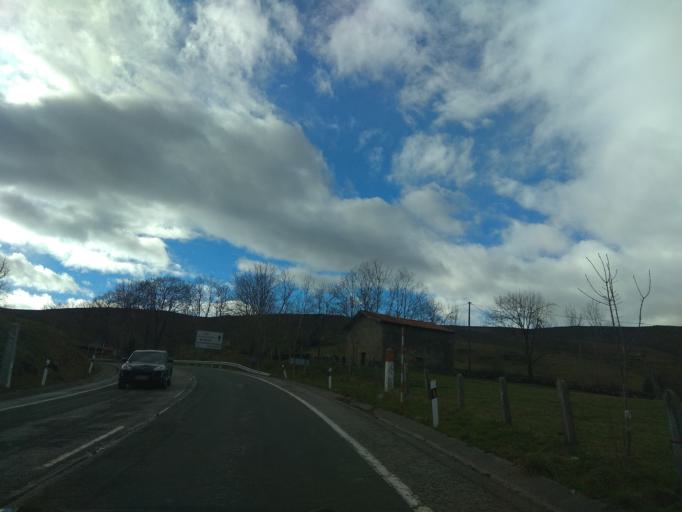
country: ES
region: Cantabria
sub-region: Provincia de Cantabria
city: San Pedro del Romeral
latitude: 43.0678
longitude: -3.8844
